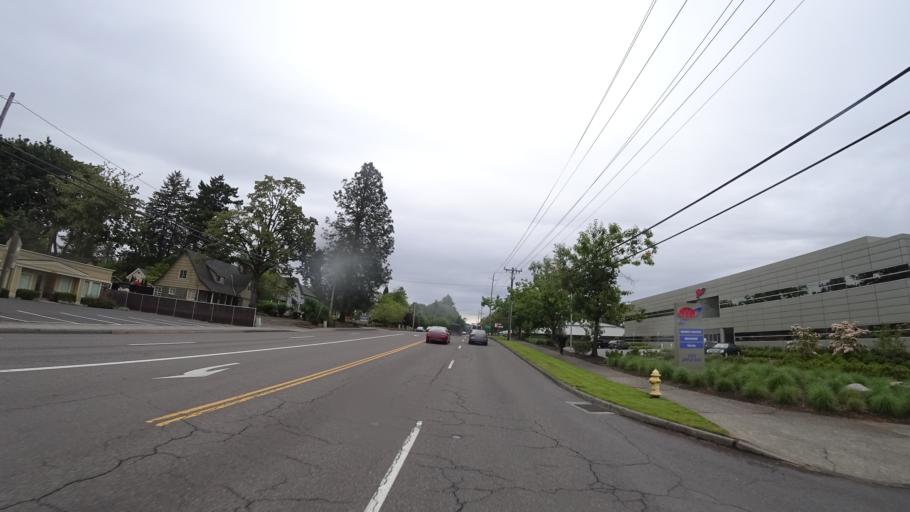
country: US
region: Oregon
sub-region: Washington County
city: Raleigh Hills
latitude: 45.4862
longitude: -122.7640
